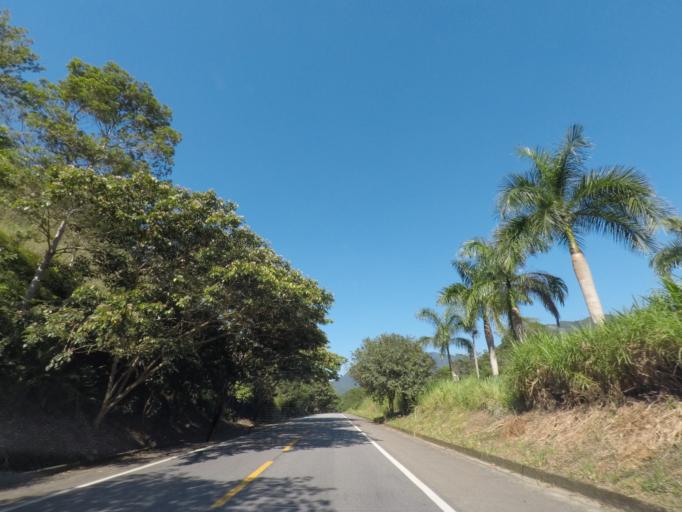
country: BR
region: Rio de Janeiro
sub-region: Parati
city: Paraty
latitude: -23.3084
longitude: -44.7074
